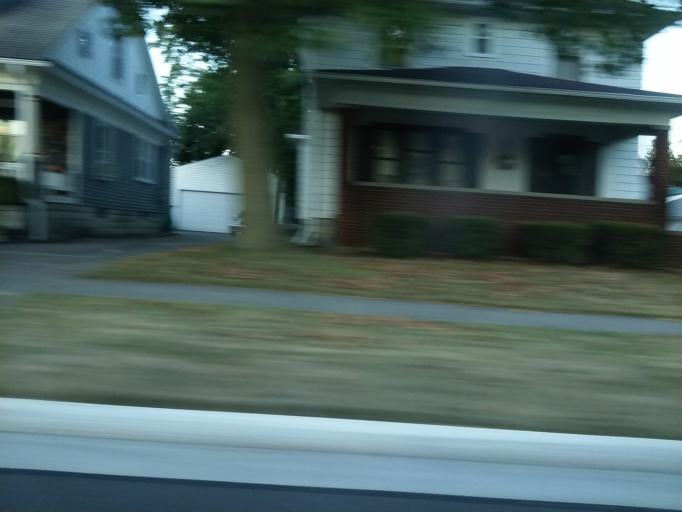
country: US
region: Ohio
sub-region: Hancock County
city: Findlay
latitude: 41.0503
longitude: -83.6500
